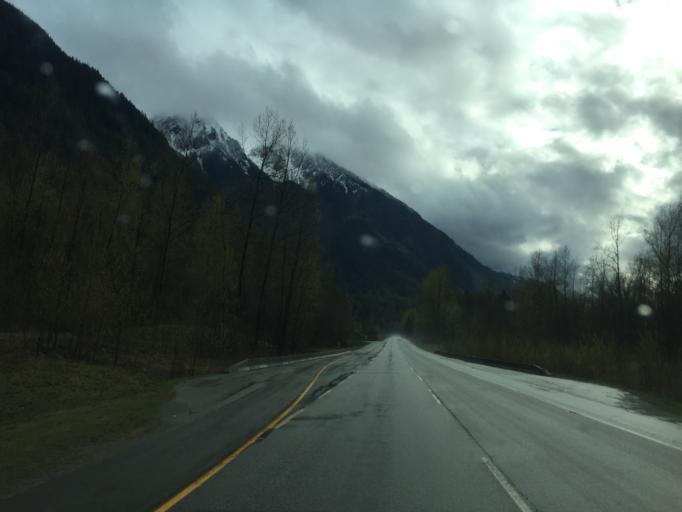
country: CA
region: British Columbia
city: Agassiz
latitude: 49.2292
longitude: -121.6849
